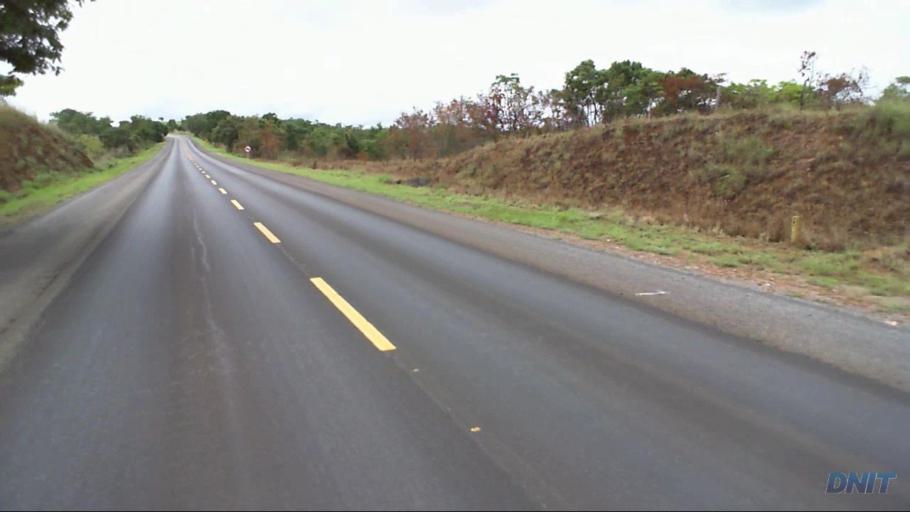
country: BR
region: Goias
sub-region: Padre Bernardo
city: Padre Bernardo
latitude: -15.2158
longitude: -48.5073
